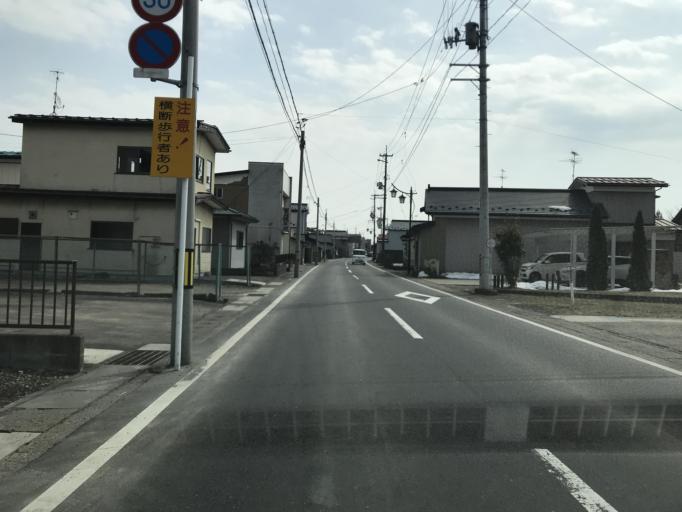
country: JP
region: Miyagi
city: Furukawa
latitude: 38.6617
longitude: 140.8650
